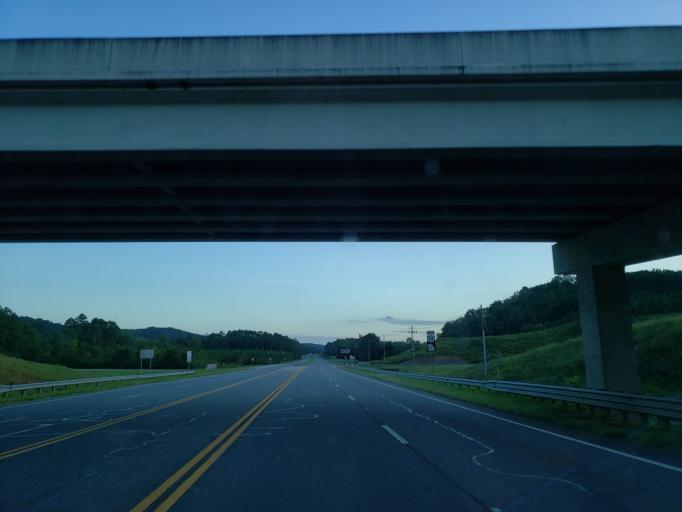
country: US
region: Georgia
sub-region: Floyd County
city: Lindale
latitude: 34.1647
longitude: -85.2126
